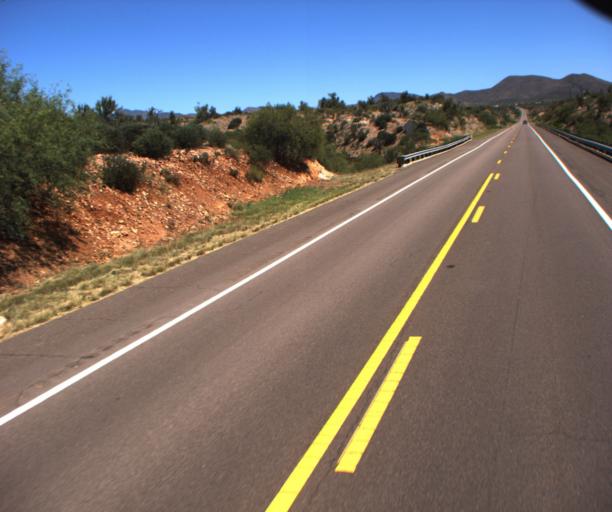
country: US
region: Arizona
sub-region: Gila County
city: Globe
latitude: 33.4142
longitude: -110.7379
